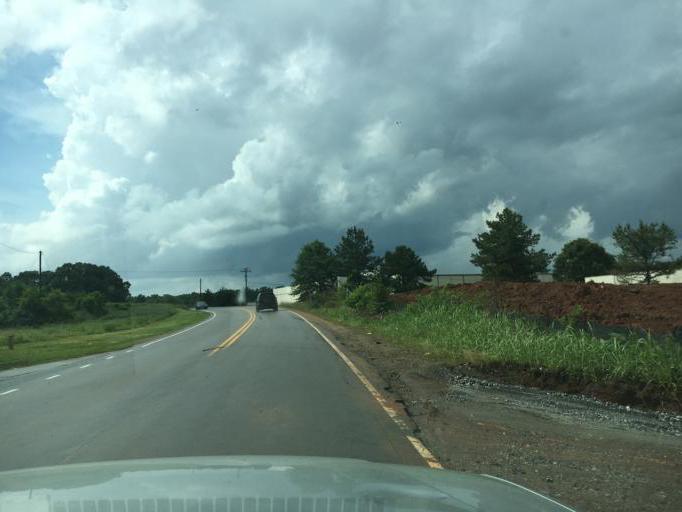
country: US
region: South Carolina
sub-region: Spartanburg County
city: Wellford
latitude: 34.9319
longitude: -82.0630
